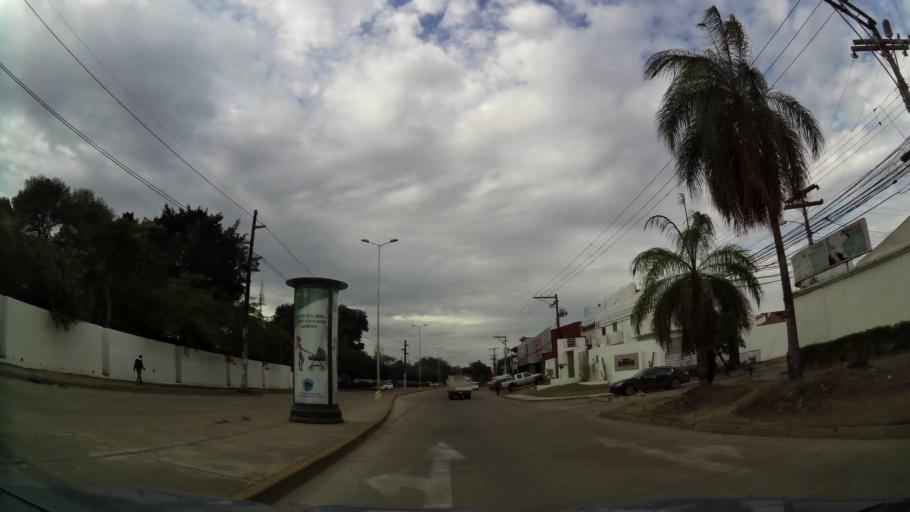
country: BO
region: Santa Cruz
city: Santa Cruz de la Sierra
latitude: -17.7660
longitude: -63.1979
